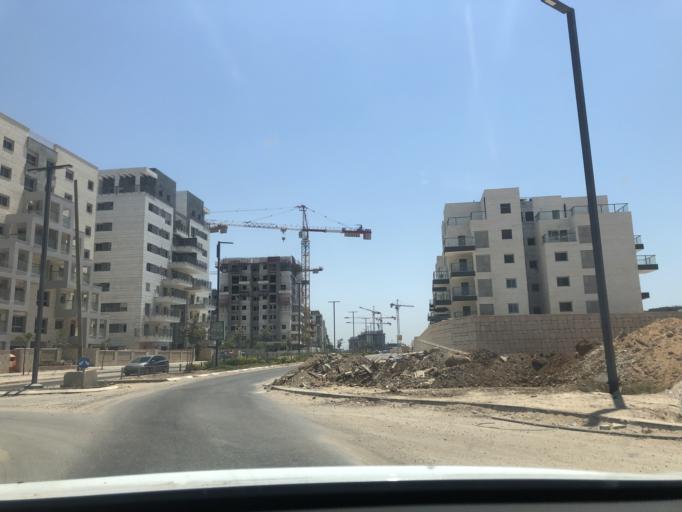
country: IL
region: Central District
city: Lod
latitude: 31.9413
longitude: 34.9003
